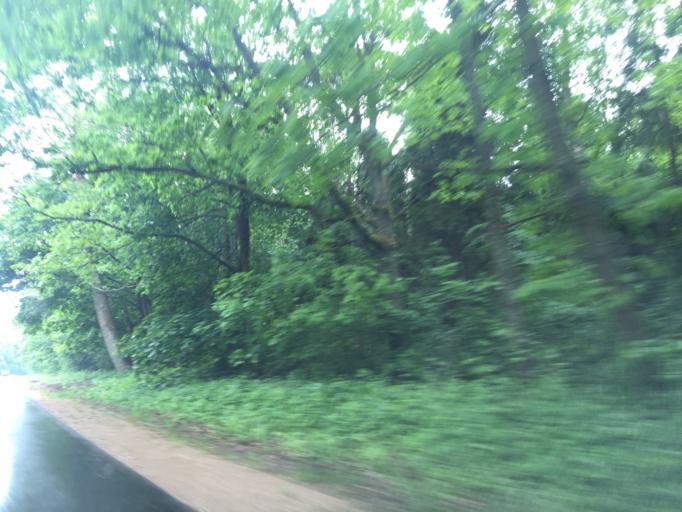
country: LT
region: Klaipedos apskritis
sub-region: Klaipeda
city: Klaipeda
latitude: 55.7794
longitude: 21.0811
